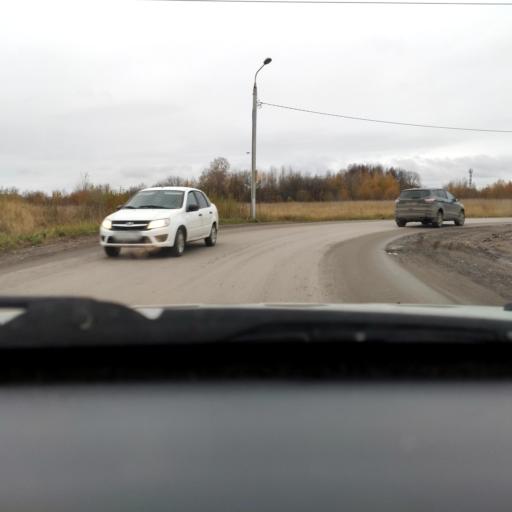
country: RU
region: Perm
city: Perm
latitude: 58.0172
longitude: 56.3354
